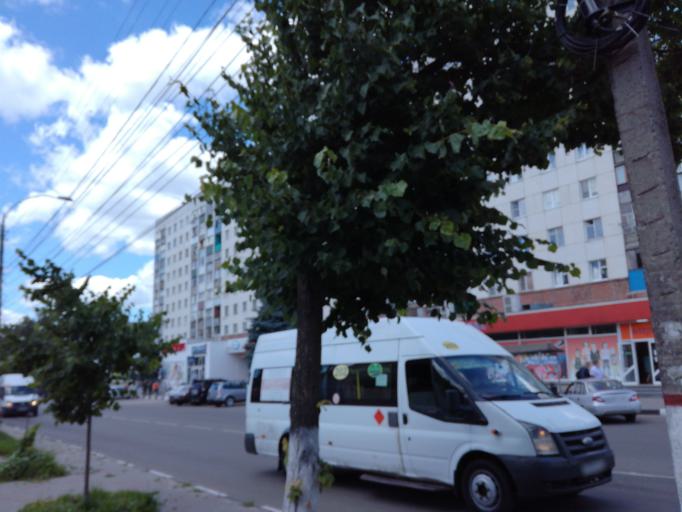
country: RU
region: Kursk
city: Kursk
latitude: 51.7468
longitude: 36.2455
